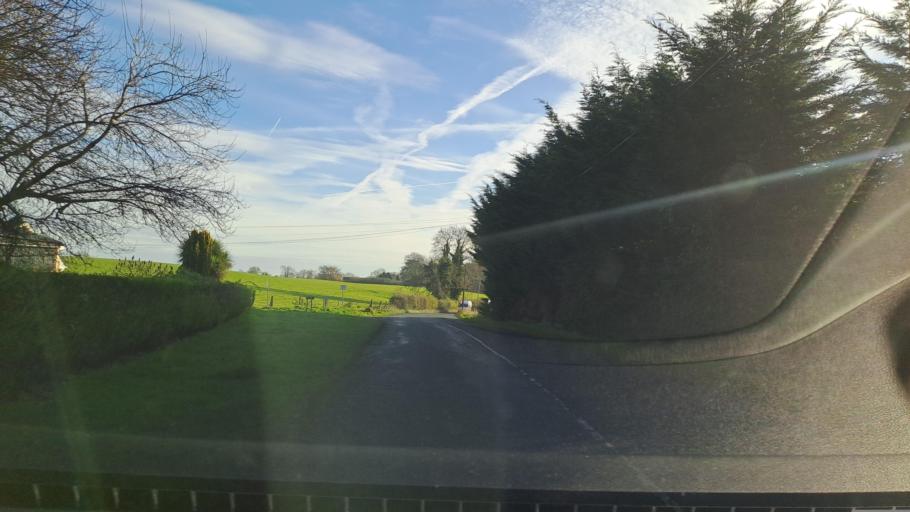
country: IE
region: Ulster
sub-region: County Monaghan
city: Carrickmacross
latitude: 53.8613
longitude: -6.6791
